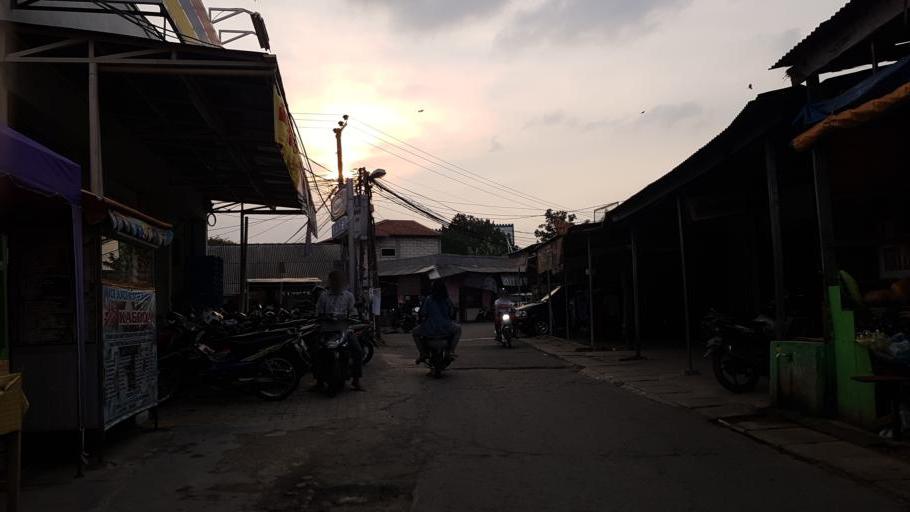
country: ID
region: West Java
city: Depok
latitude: -6.3819
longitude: 106.8037
